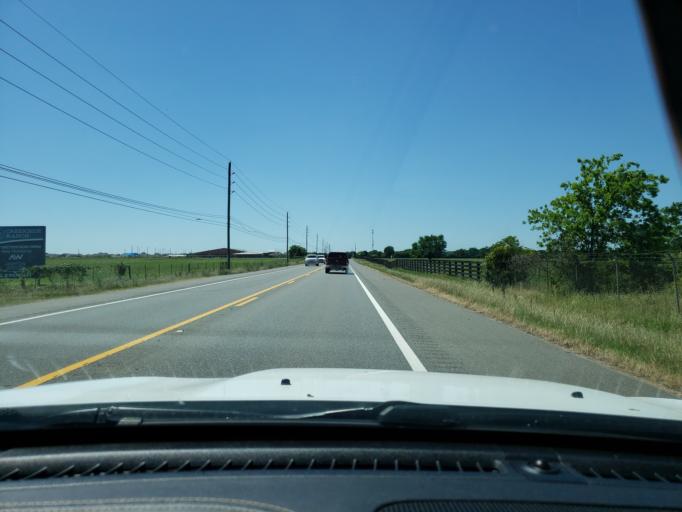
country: US
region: Texas
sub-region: Fort Bend County
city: Fulshear
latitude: 29.6763
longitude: -95.8390
